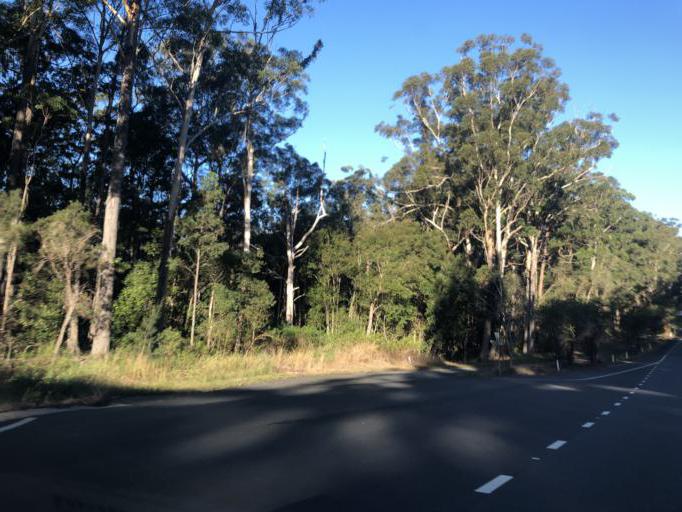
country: AU
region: New South Wales
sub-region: Nambucca Shire
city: Nambucca
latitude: -30.5471
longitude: 153.0075
